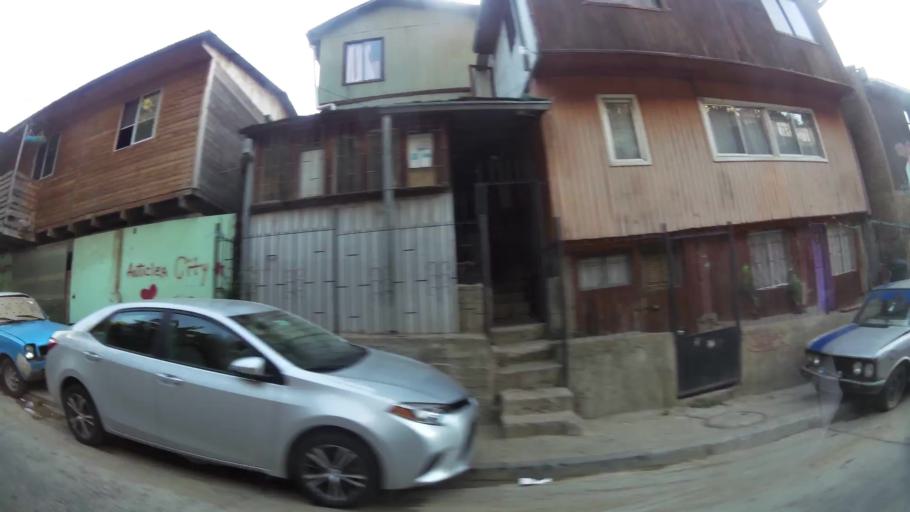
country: CL
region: Valparaiso
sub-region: Provincia de Valparaiso
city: Valparaiso
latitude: -33.0567
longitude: -71.6062
